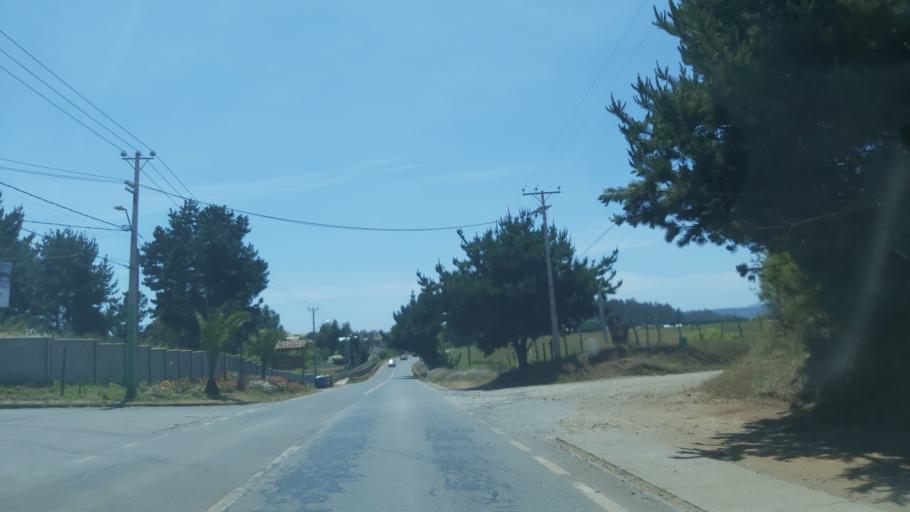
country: CL
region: Maule
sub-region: Provincia de Cauquenes
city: Cauquenes
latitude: -35.8013
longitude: -72.5650
